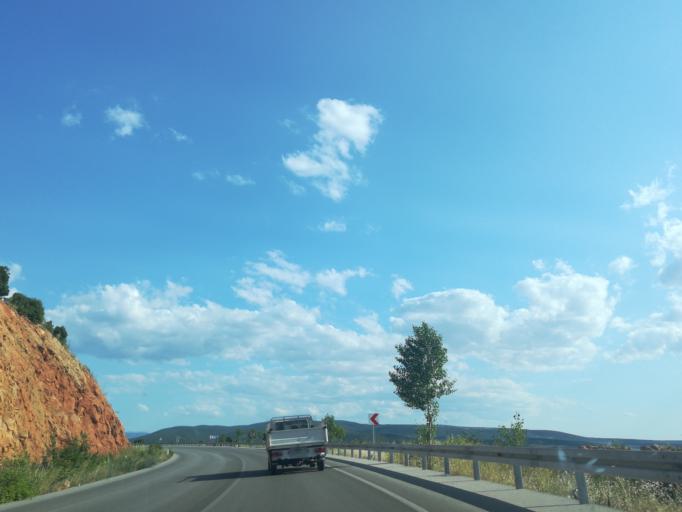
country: TR
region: Denizli
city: Ishakli
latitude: 38.1571
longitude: 30.0833
